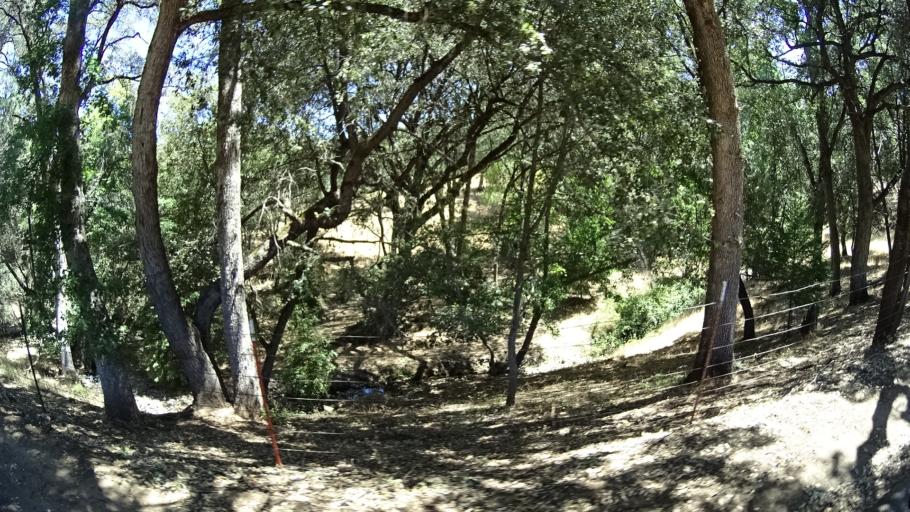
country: US
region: California
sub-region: Calaveras County
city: Forest Meadows
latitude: 38.1364
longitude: -120.4116
